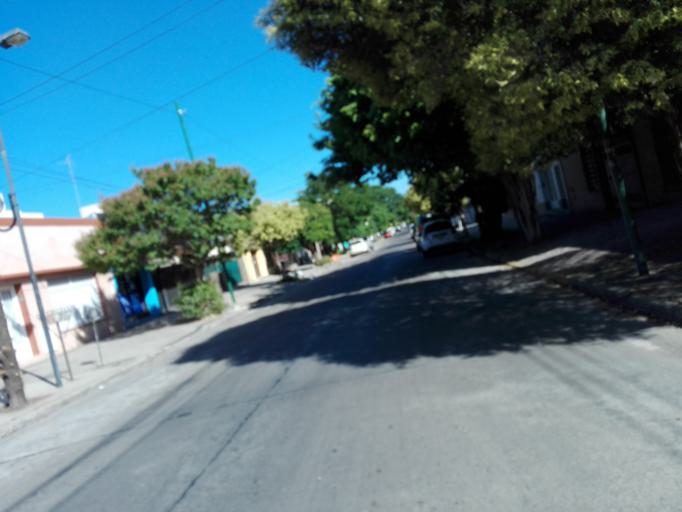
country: AR
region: Buenos Aires
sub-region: Partido de La Plata
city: La Plata
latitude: -34.9433
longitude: -57.9573
